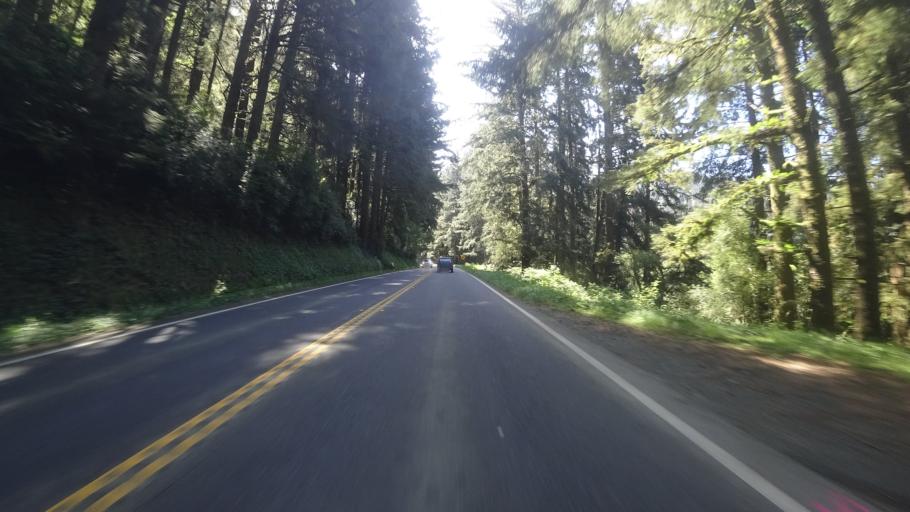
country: US
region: California
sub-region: Del Norte County
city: Bertsch-Oceanview
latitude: 41.5867
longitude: -124.0926
